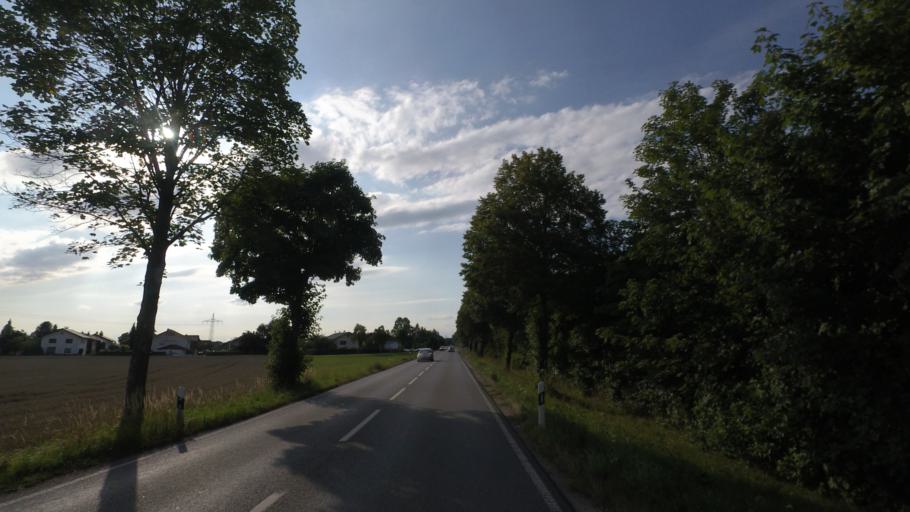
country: DE
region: Bavaria
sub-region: Upper Bavaria
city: Chieming
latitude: 47.9053
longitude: 12.5413
